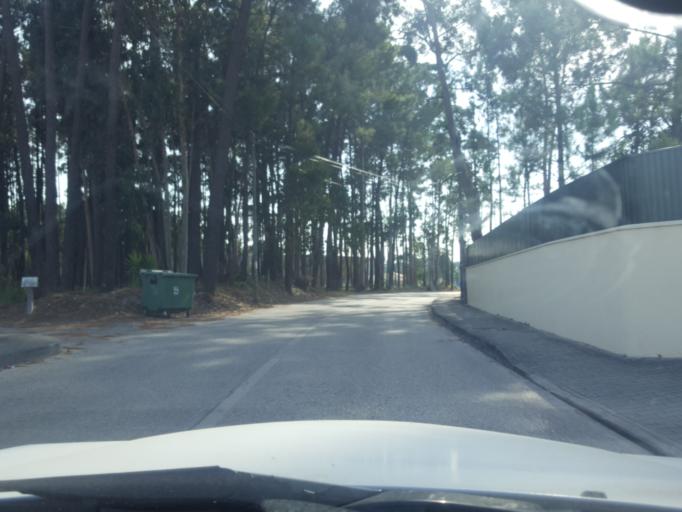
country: PT
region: Leiria
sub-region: Leiria
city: Leiria
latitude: 39.7288
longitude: -8.7643
